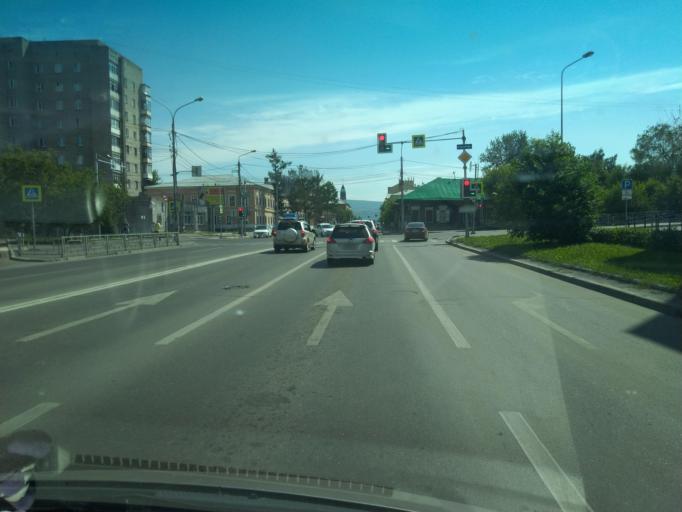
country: RU
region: Krasnoyarskiy
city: Krasnoyarsk
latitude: 56.0155
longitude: 92.8706
